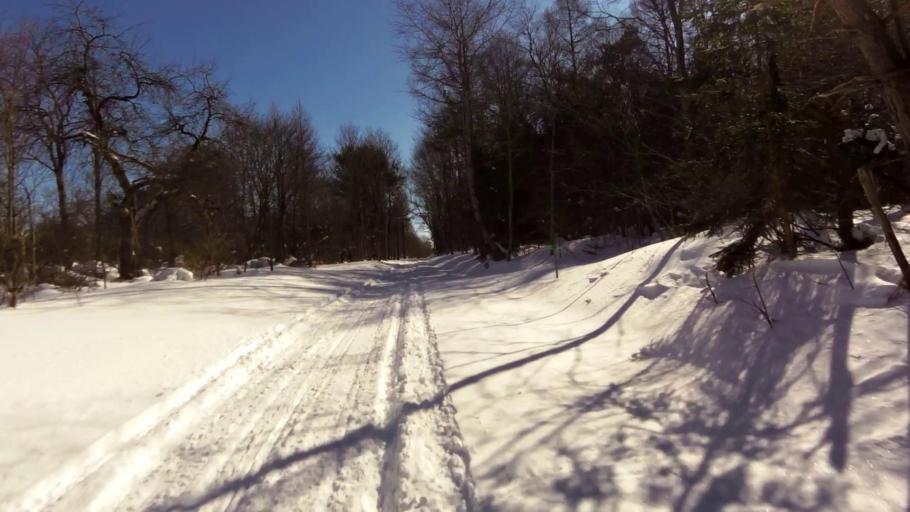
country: US
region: New York
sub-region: Cattaraugus County
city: Franklinville
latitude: 42.3432
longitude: -78.3599
